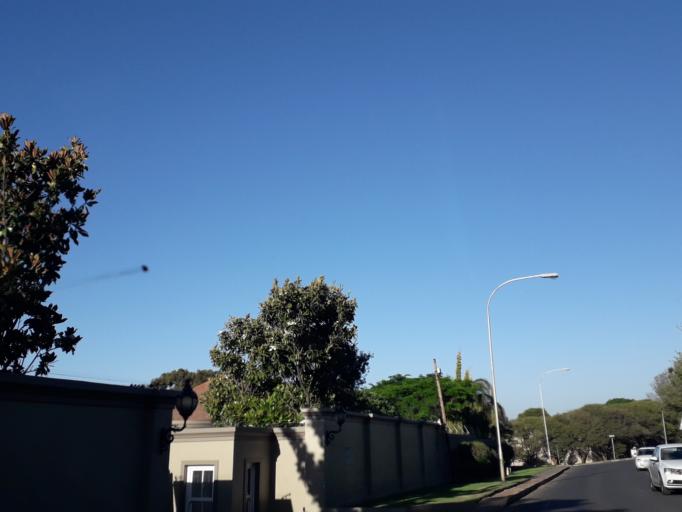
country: ZA
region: Gauteng
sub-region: City of Johannesburg Metropolitan Municipality
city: Johannesburg
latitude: -26.1399
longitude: 27.9684
